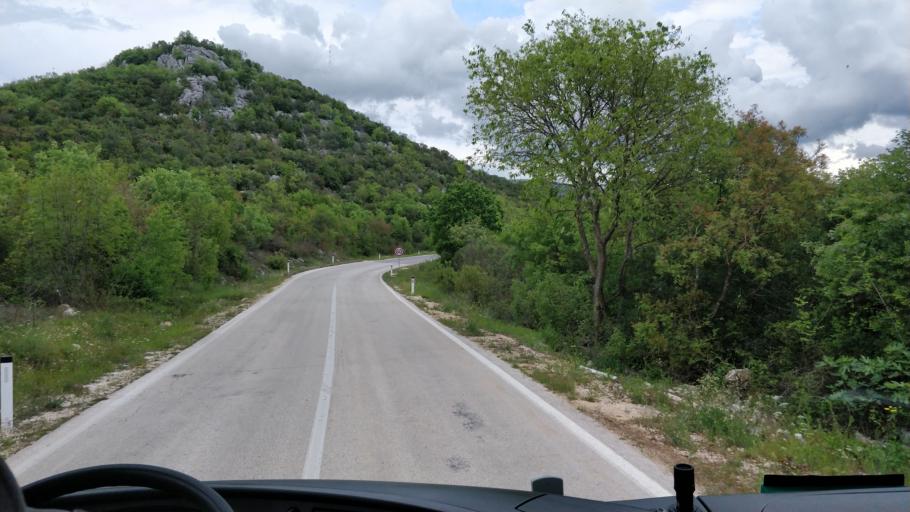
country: BA
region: Federation of Bosnia and Herzegovina
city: Vitina
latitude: 43.1732
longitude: 17.4843
